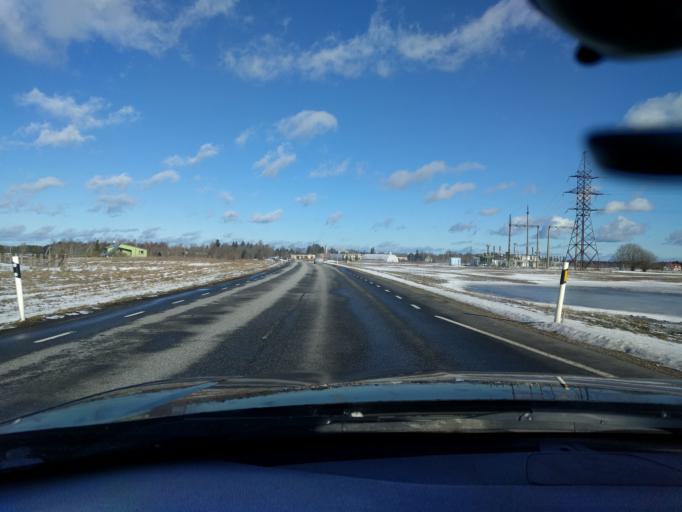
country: EE
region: Harju
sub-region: Raasiku vald
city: Raasiku
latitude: 59.3708
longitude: 25.1929
